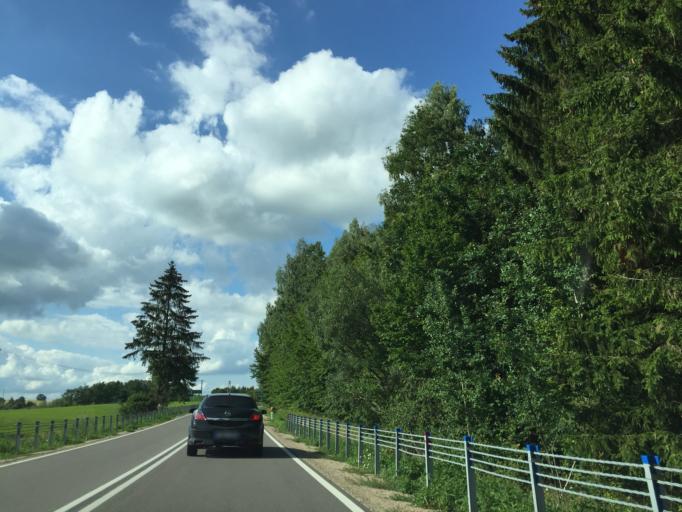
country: PL
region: Podlasie
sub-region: Powiat sejnenski
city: Punsk
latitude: 54.2395
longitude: 23.0985
